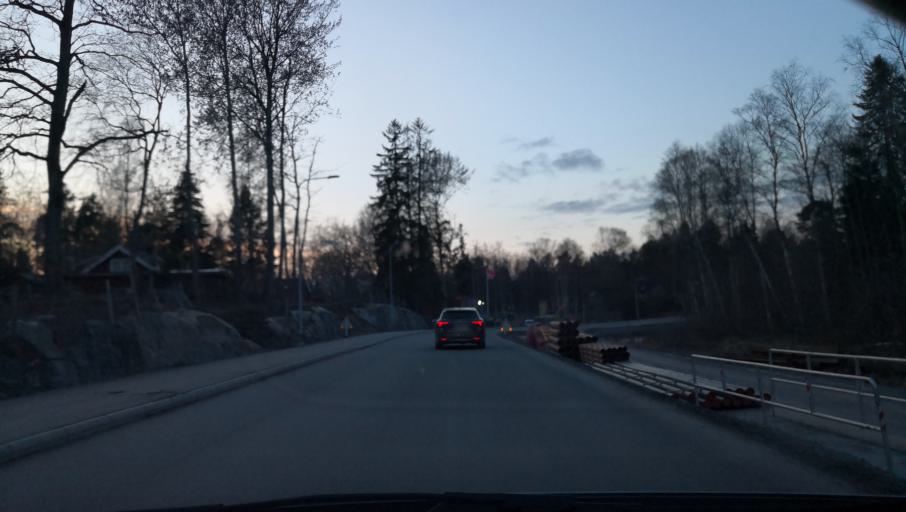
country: SE
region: Stockholm
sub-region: Nacka Kommun
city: Kummelnas
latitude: 59.3491
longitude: 18.2899
